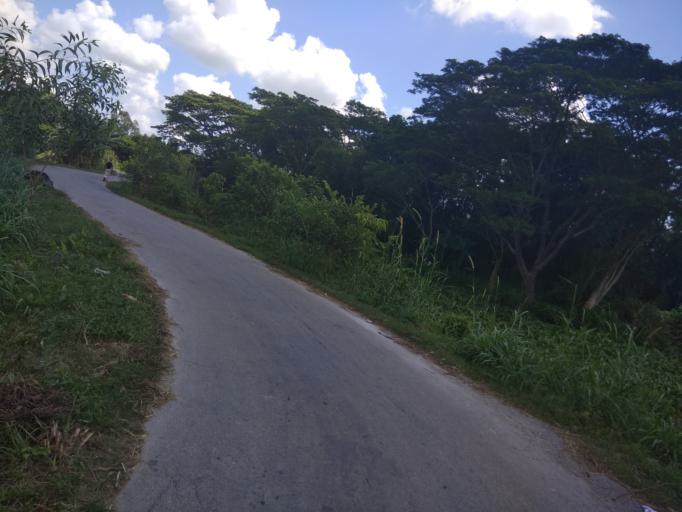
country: BD
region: Dhaka
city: Narayanganj
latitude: 23.4498
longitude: 90.4773
